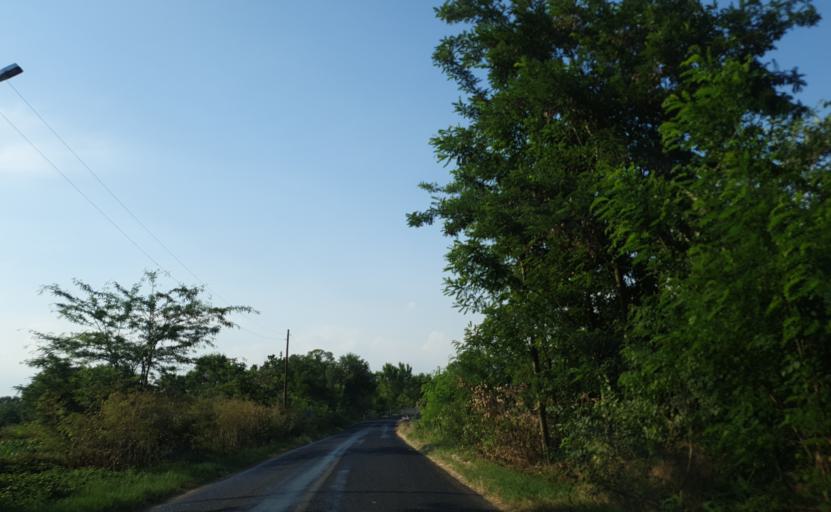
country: TR
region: Tekirdag
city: Muratli
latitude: 41.1971
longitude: 27.4700
